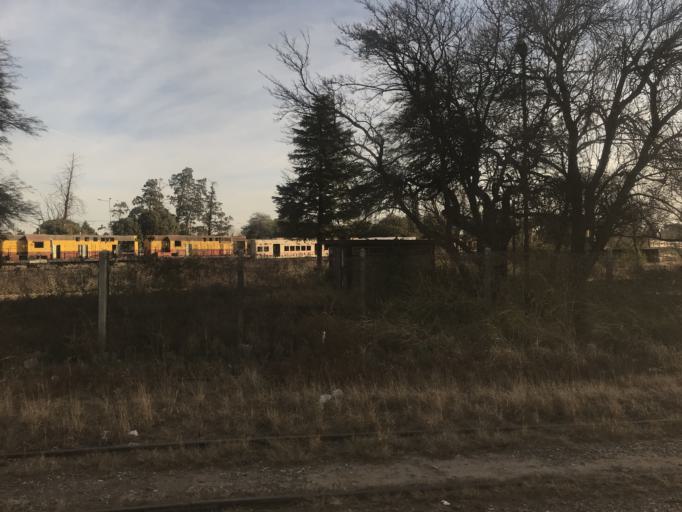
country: AR
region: Cordoba
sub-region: Departamento de Capital
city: Cordoba
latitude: -31.4593
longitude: -64.1091
